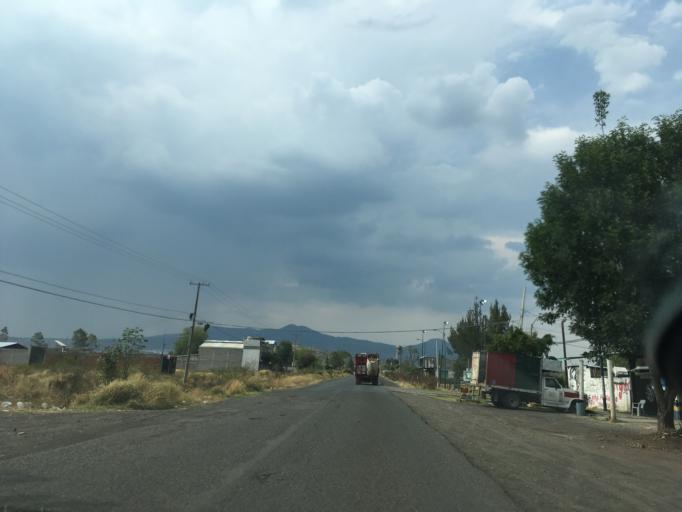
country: MX
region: Michoacan
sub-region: Morelia
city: La Mintzita (Piedra Dura)
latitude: 19.6524
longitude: -101.2798
